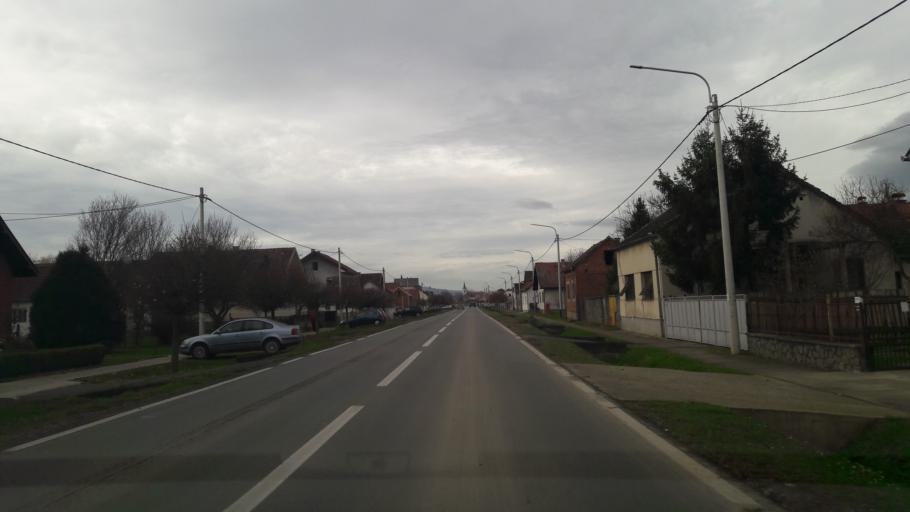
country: HR
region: Osjecko-Baranjska
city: Fericanci
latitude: 45.5237
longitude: 17.9896
